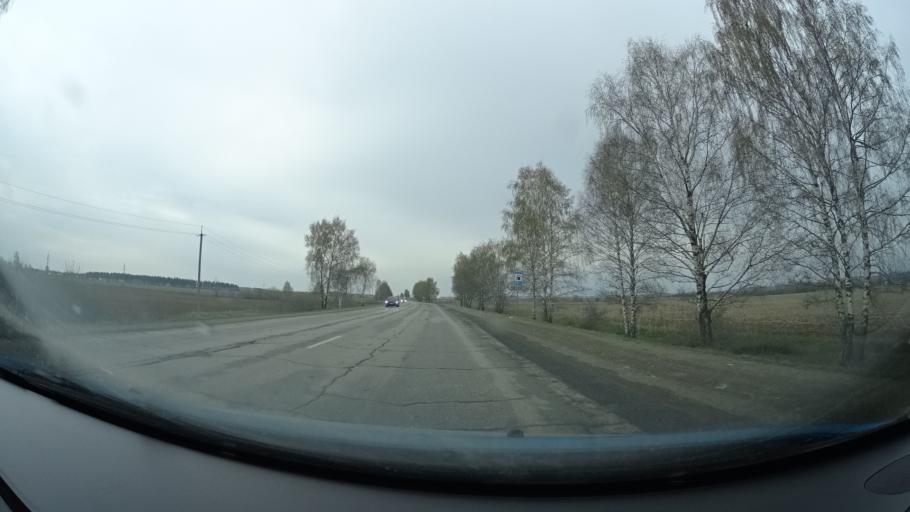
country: RU
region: Perm
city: Ust'-Kachka
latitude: 58.0739
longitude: 55.6387
